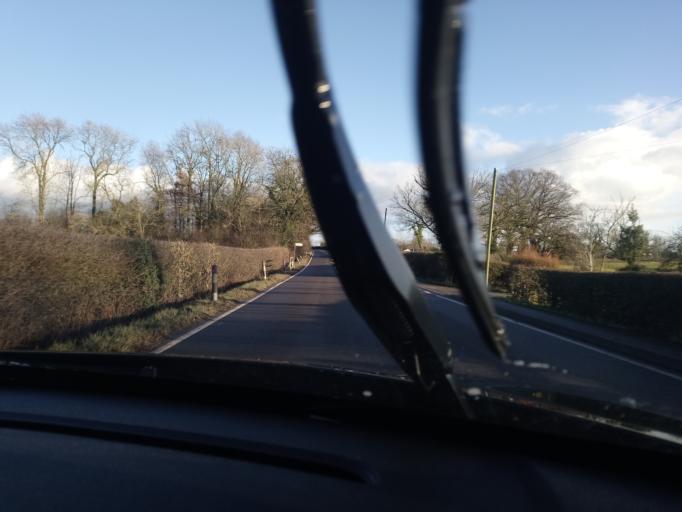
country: GB
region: Wales
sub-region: Wrexham
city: Overton
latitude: 52.9264
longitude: -2.9498
